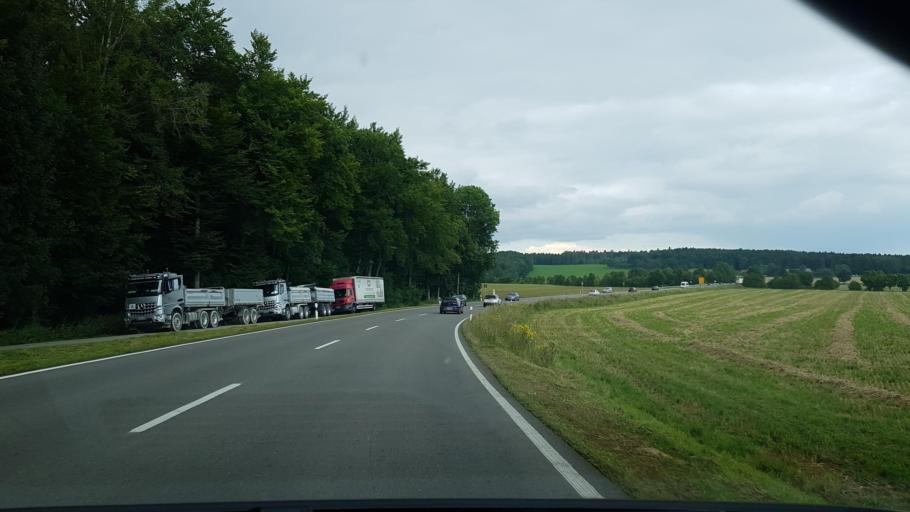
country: DE
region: Baden-Wuerttemberg
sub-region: Tuebingen Region
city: Laichingen
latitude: 48.4639
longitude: 9.6617
